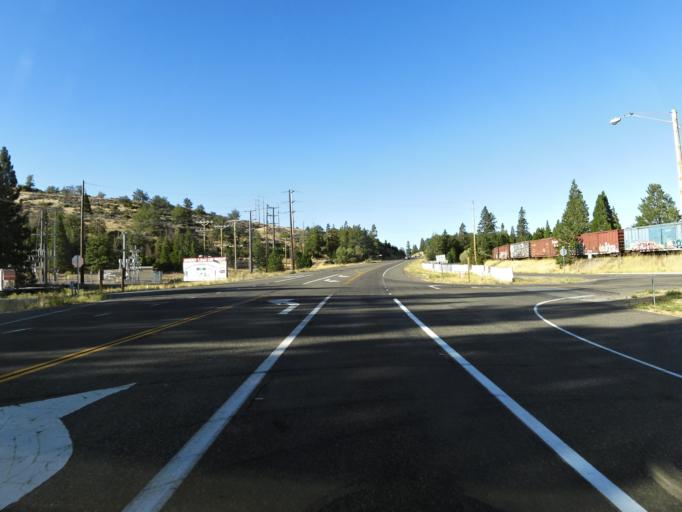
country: US
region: California
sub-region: Siskiyou County
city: Weed
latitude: 41.4302
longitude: -122.3891
